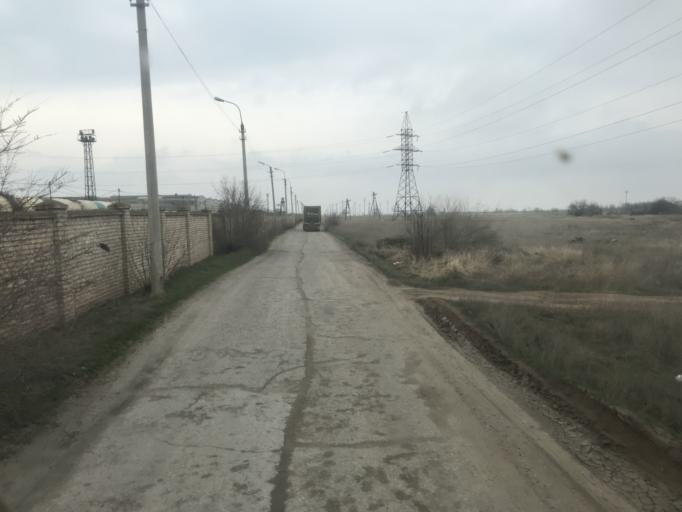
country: RU
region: Volgograd
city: Krasnoslobodsk
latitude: 48.5320
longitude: 44.5867
